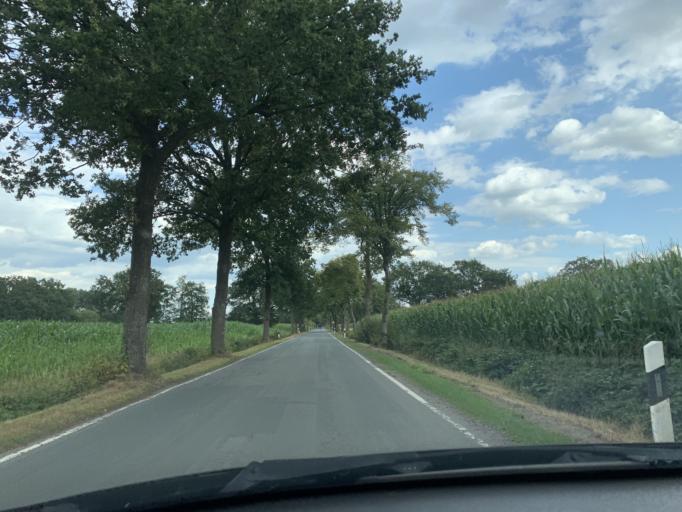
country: DE
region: Lower Saxony
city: Apen
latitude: 53.2209
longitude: 7.8616
